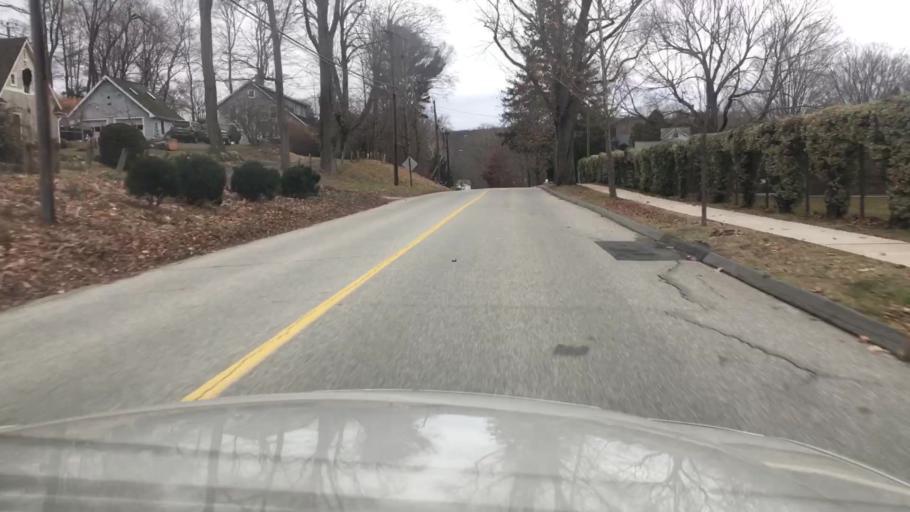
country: US
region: Connecticut
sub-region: Middlesex County
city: Essex Village
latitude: 41.3587
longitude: -72.3955
